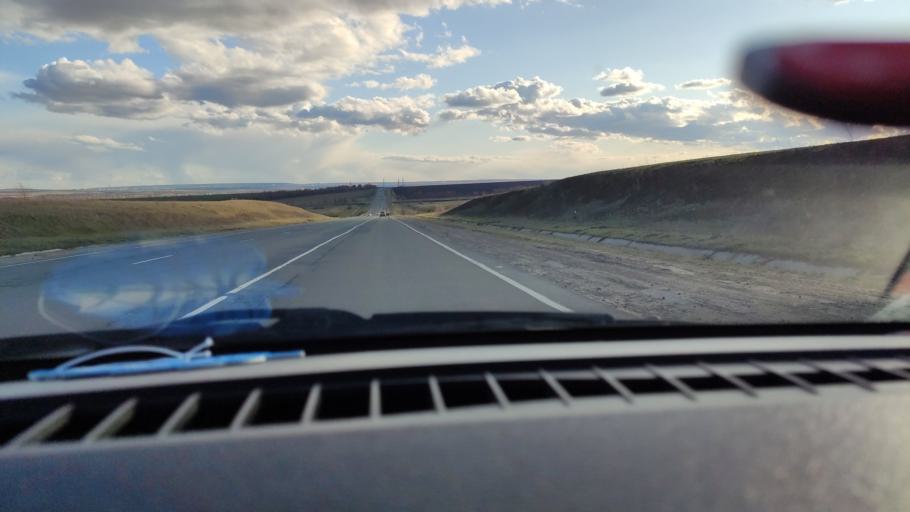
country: RU
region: Saratov
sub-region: Saratovskiy Rayon
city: Saratov
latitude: 51.7553
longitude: 46.0650
